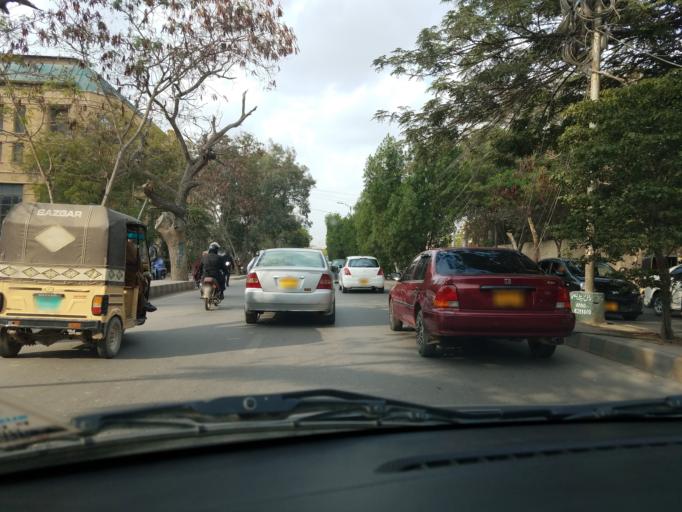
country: PK
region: Sindh
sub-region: Karachi District
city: Karachi
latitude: 24.8444
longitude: 67.0321
